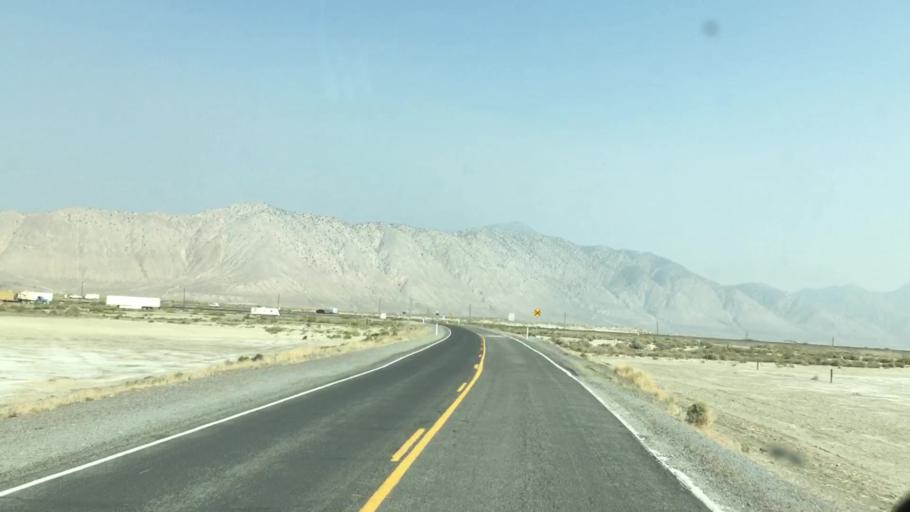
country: US
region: Nevada
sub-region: Pershing County
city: Lovelock
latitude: 40.6521
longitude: -119.3449
